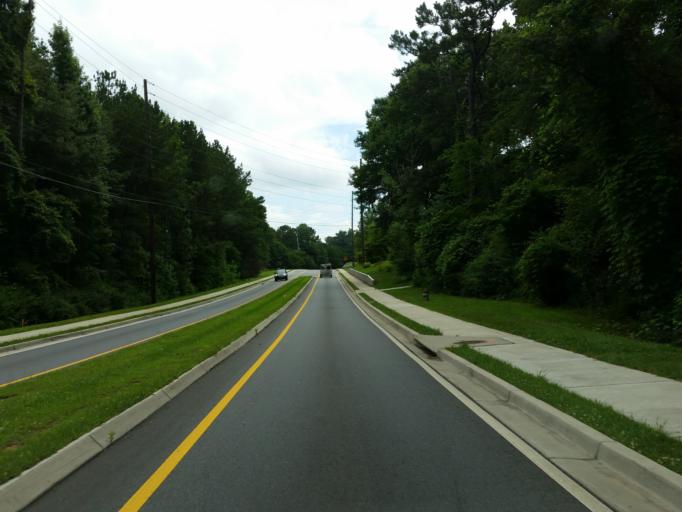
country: US
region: Georgia
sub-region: Cobb County
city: Kennesaw
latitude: 34.0453
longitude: -84.6250
